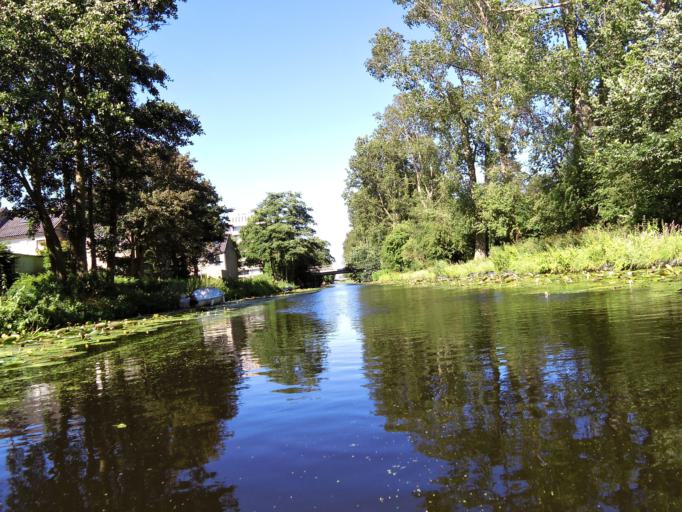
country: NL
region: South Holland
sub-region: Gemeente Wassenaar
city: Wassenaar
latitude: 52.1468
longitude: 4.4074
